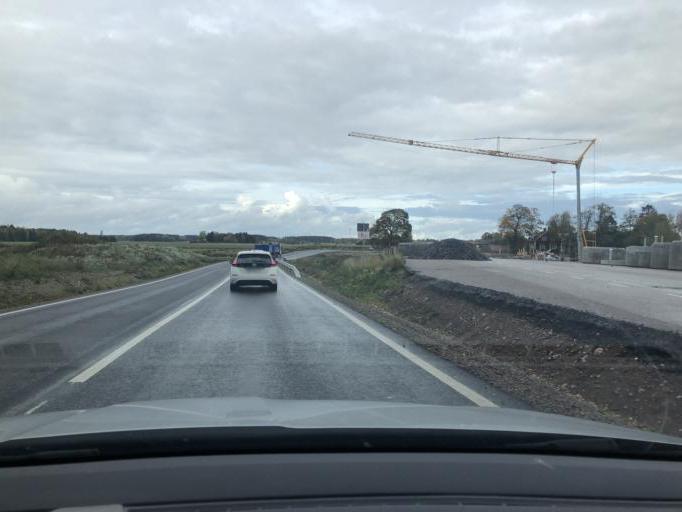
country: SE
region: Vaestra Goetaland
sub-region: Skara Kommun
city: Skara
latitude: 58.4177
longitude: 13.4659
